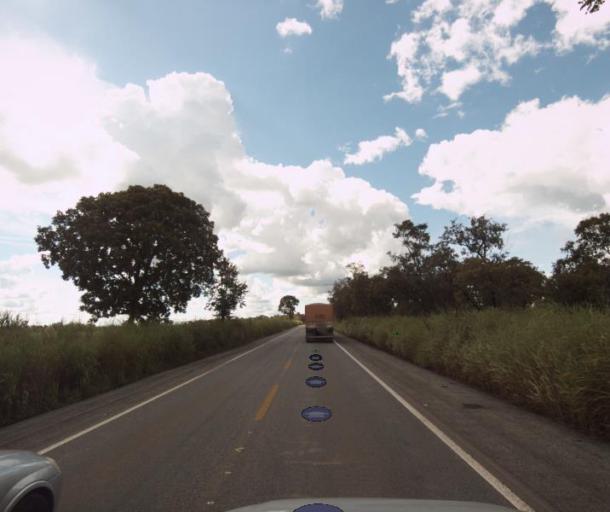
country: BR
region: Goias
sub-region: Porangatu
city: Porangatu
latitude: -13.2239
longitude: -49.1478
